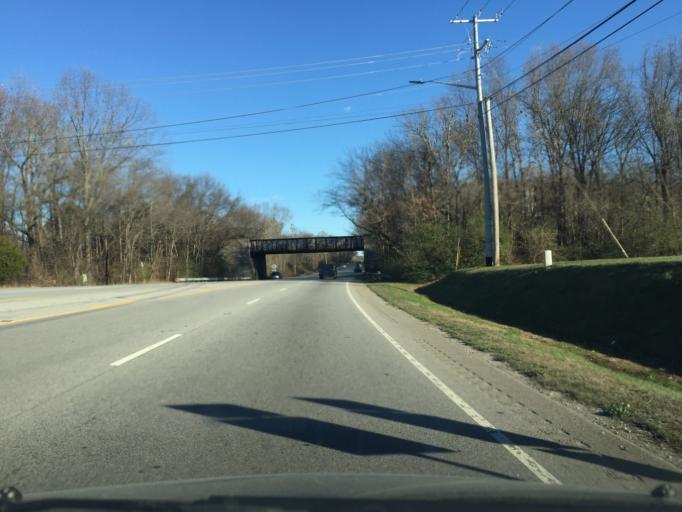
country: US
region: Tennessee
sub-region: Hamilton County
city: East Chattanooga
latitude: 35.0962
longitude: -85.2367
